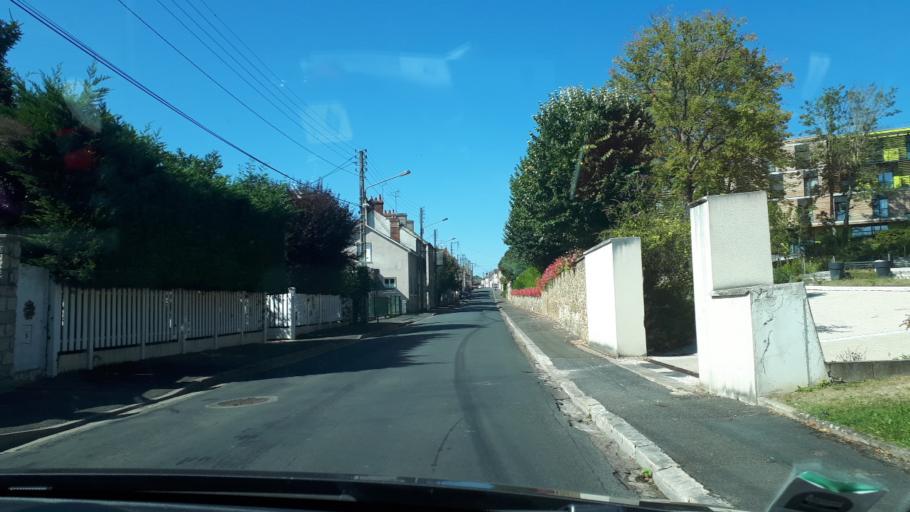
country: FR
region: Centre
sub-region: Departement du Loiret
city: Briare
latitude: 47.5907
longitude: 2.7470
